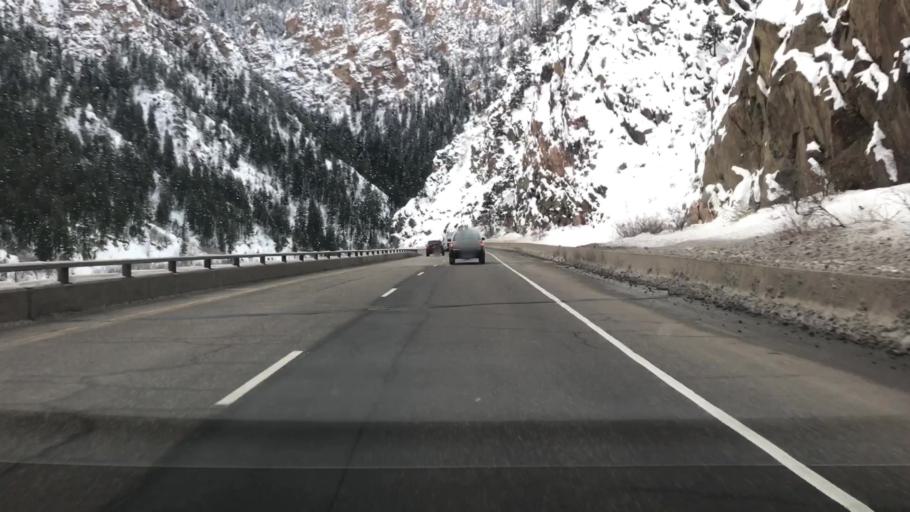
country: US
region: Colorado
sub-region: Garfield County
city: Glenwood Springs
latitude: 39.5602
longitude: -107.2407
